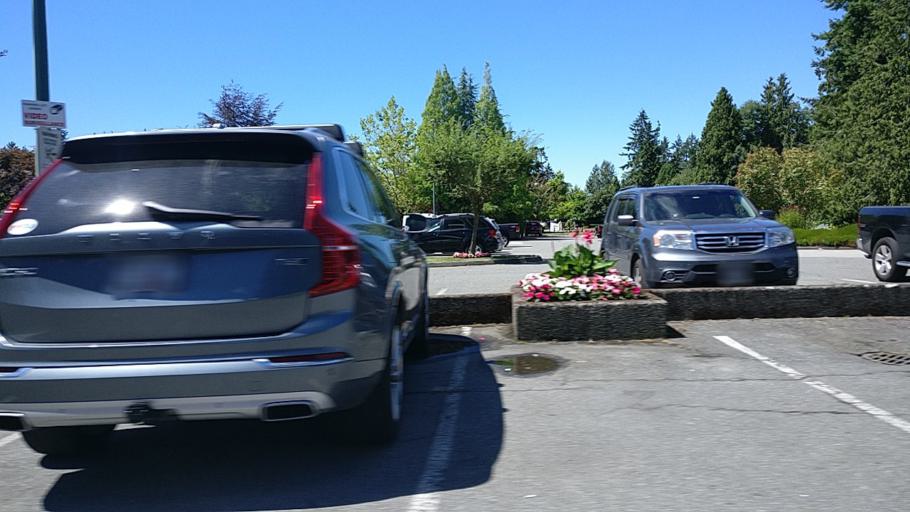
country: US
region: Washington
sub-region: Whatcom County
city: Blaine
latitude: 49.0160
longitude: -122.7198
